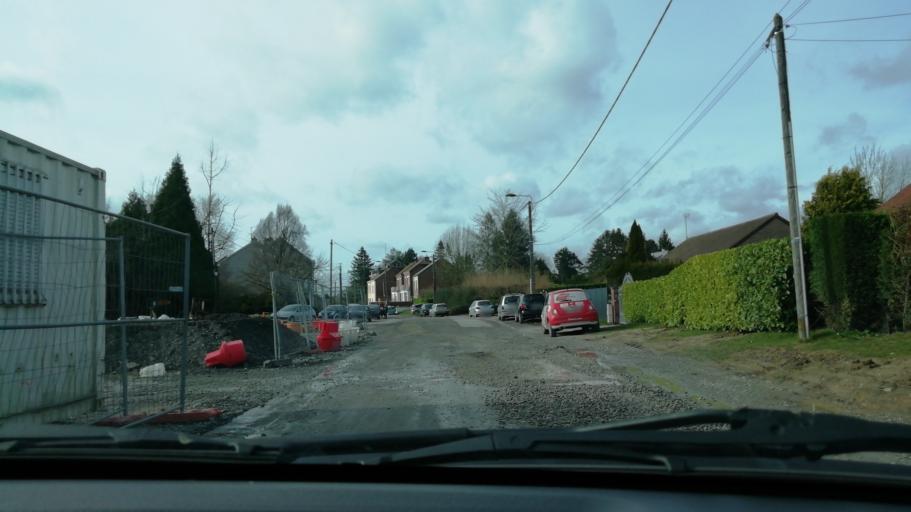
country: FR
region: Nord-Pas-de-Calais
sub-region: Departement du Nord
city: Louvroil
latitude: 50.2790
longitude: 3.9505
